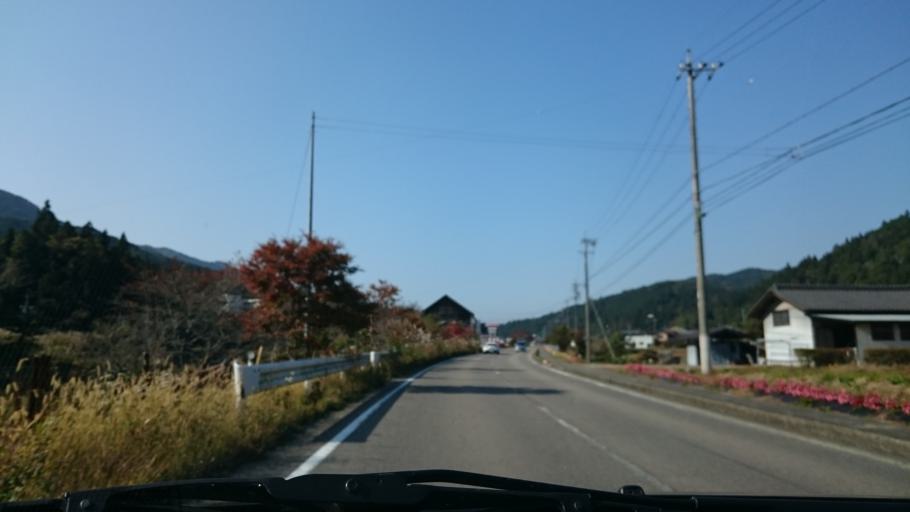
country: JP
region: Gifu
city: Nakatsugawa
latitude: 35.7144
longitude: 137.3676
